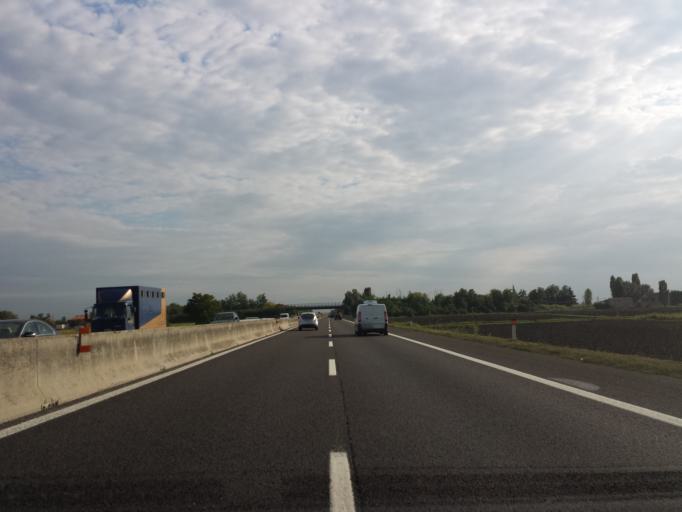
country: IT
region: Veneto
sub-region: Provincia di Padova
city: Stanghella
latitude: 45.1590
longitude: 11.7756
